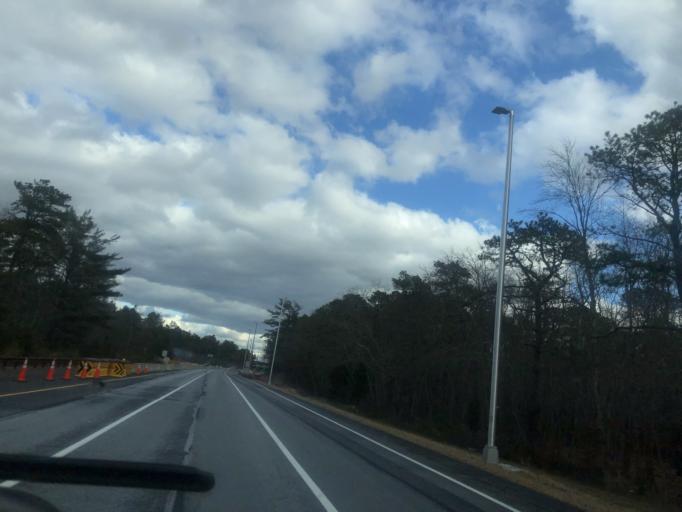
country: US
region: New Jersey
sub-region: Ocean County
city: Mystic Island
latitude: 39.6107
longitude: -74.4277
